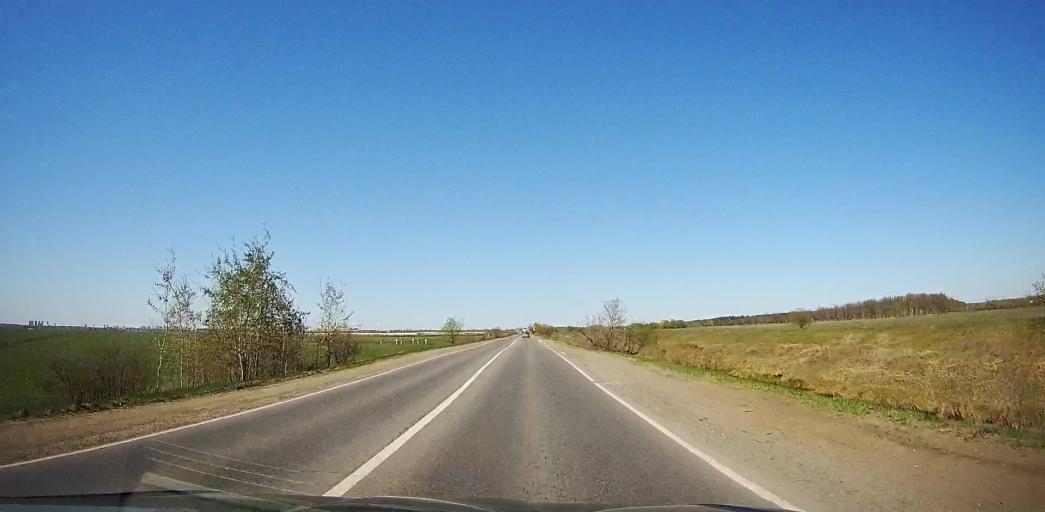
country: RU
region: Moskovskaya
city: Ramenskoye
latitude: 55.5190
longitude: 38.2758
